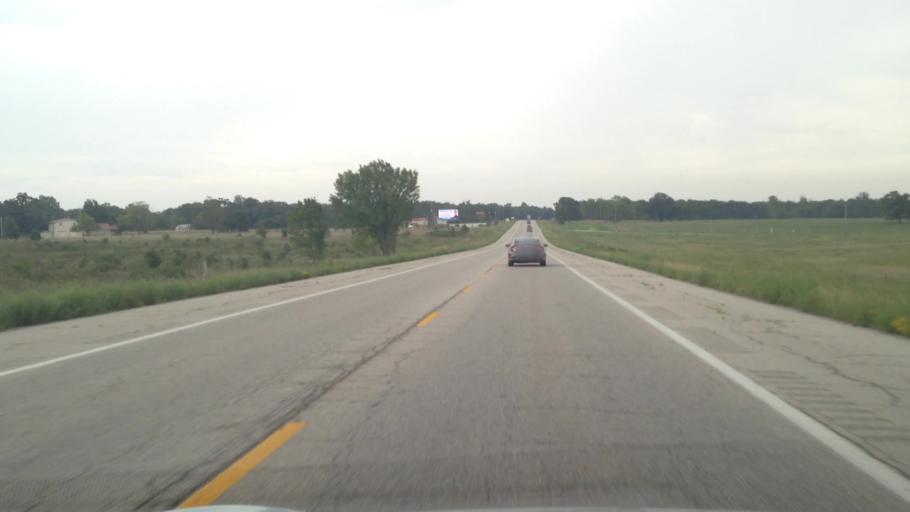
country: US
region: Kansas
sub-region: Cherokee County
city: Galena
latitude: 37.0116
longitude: -94.6273
